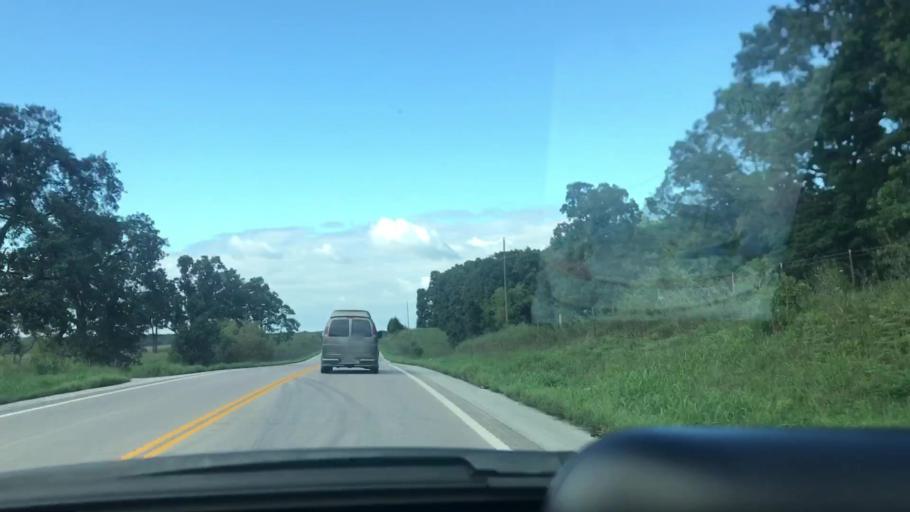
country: US
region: Missouri
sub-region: Hickory County
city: Hermitage
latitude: 37.9637
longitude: -93.2067
